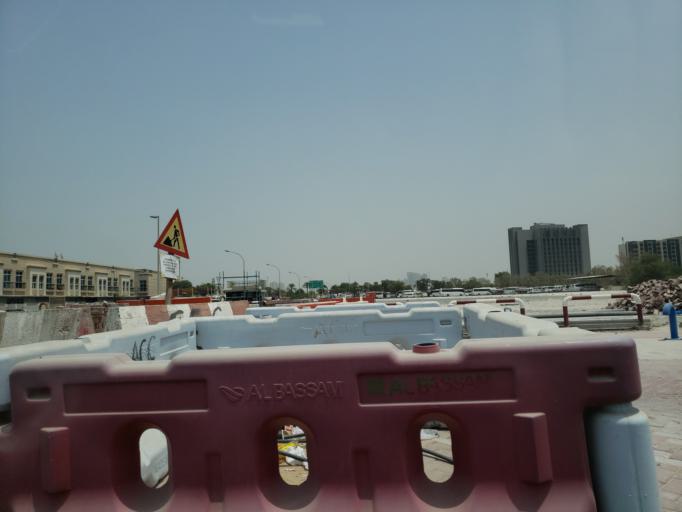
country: AE
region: Ash Shariqah
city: Sharjah
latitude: 25.2295
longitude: 55.2820
